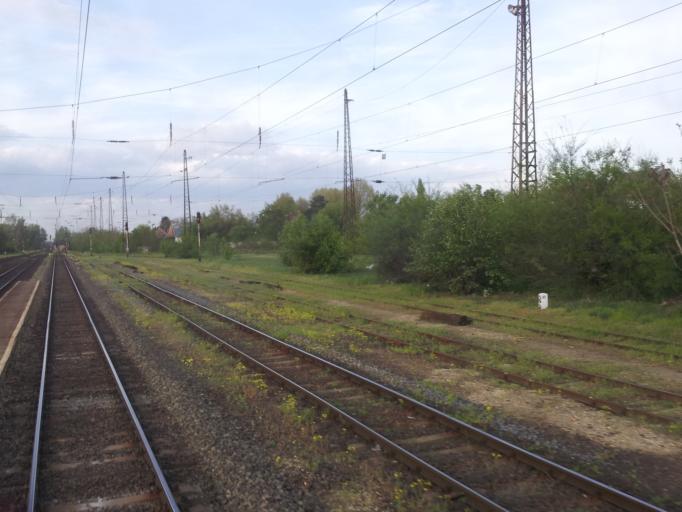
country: HU
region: Budapest
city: Budapest XV. keruelet
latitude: 47.5688
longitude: 19.1138
